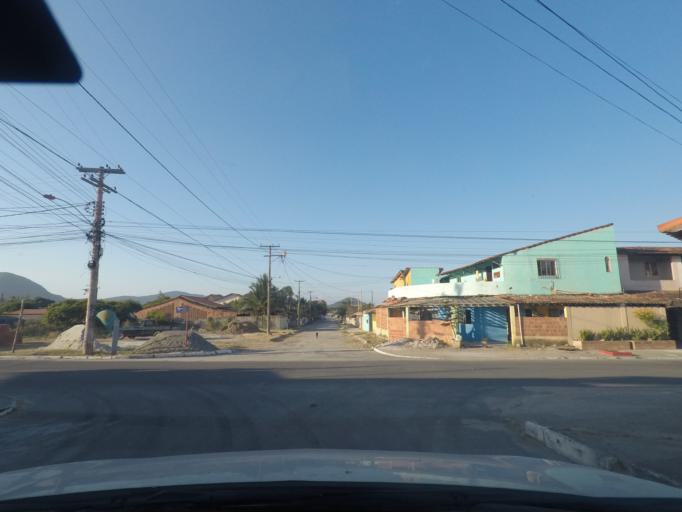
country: BR
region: Rio de Janeiro
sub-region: Marica
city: Marica
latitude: -22.9671
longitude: -42.9316
